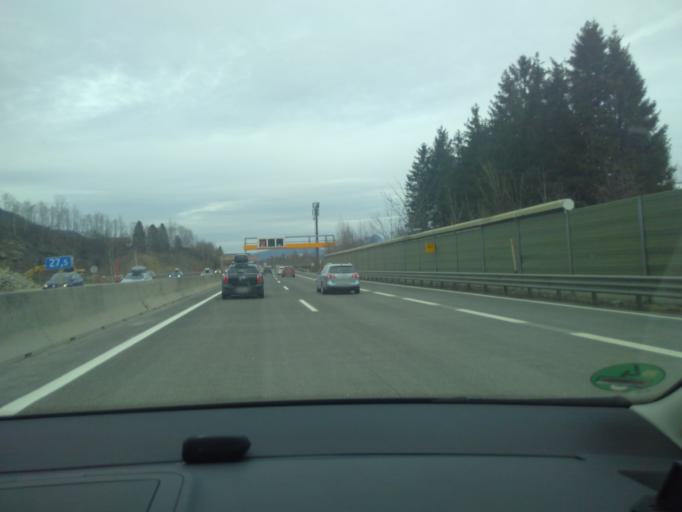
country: AT
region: Salzburg
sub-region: Politischer Bezirk Hallein
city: Golling an der Salzach
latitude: 47.5947
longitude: 13.1518
